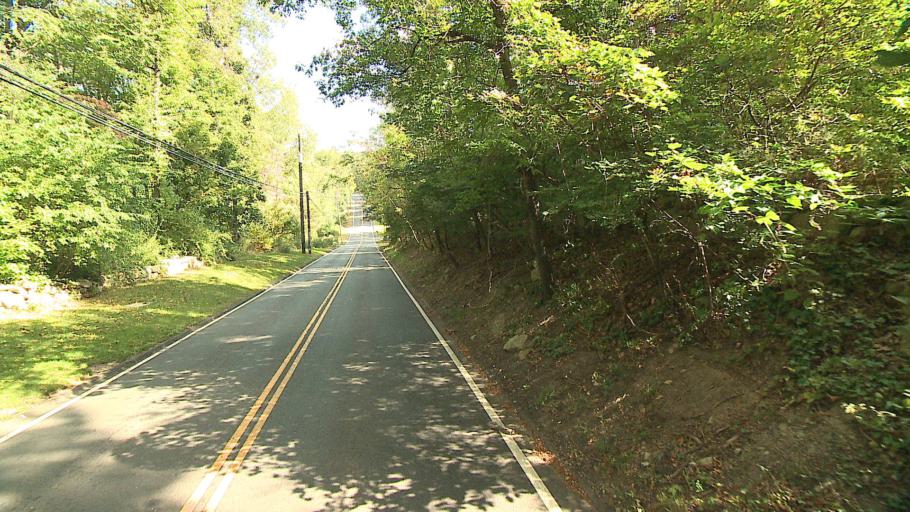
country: US
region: Connecticut
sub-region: Fairfield County
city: Wilton
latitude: 41.1799
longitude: -73.4271
